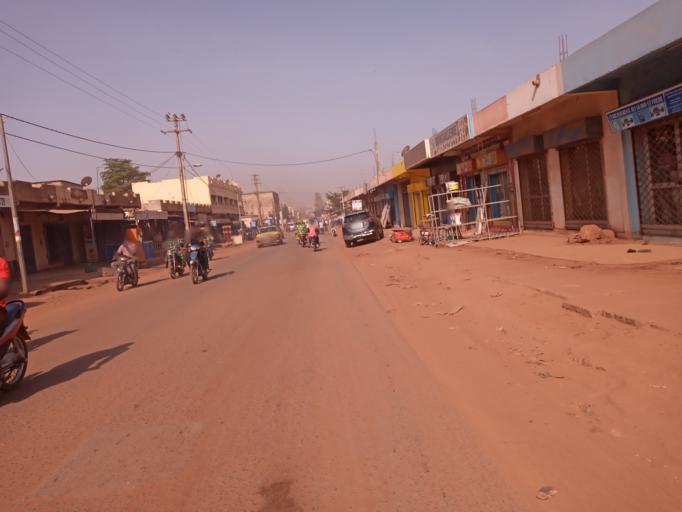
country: ML
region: Bamako
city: Bamako
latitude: 12.5884
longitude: -7.9719
